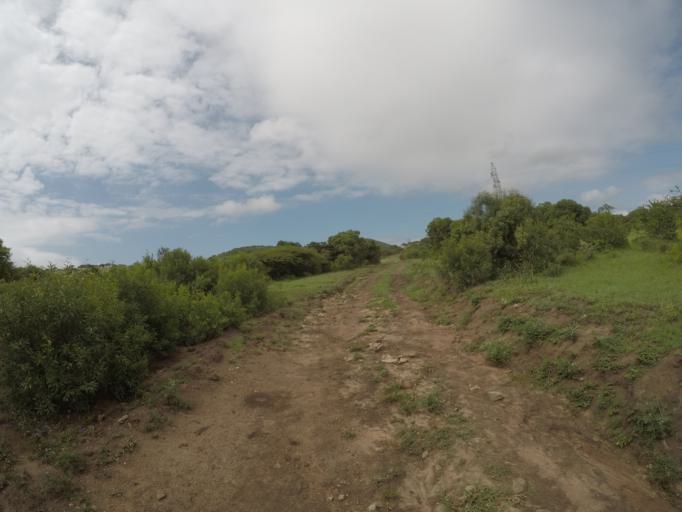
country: ZA
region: KwaZulu-Natal
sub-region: uThungulu District Municipality
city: Empangeni
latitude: -28.6226
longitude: 31.8653
